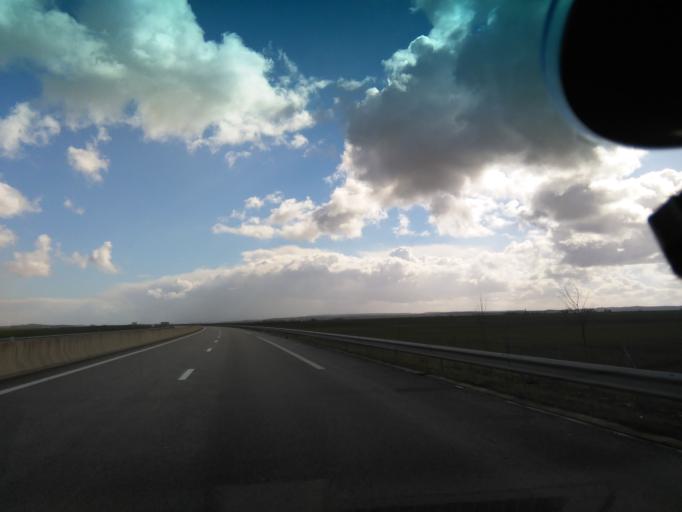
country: FR
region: Lower Normandy
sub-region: Departement de l'Orne
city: Argentan
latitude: 48.7073
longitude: -0.0502
